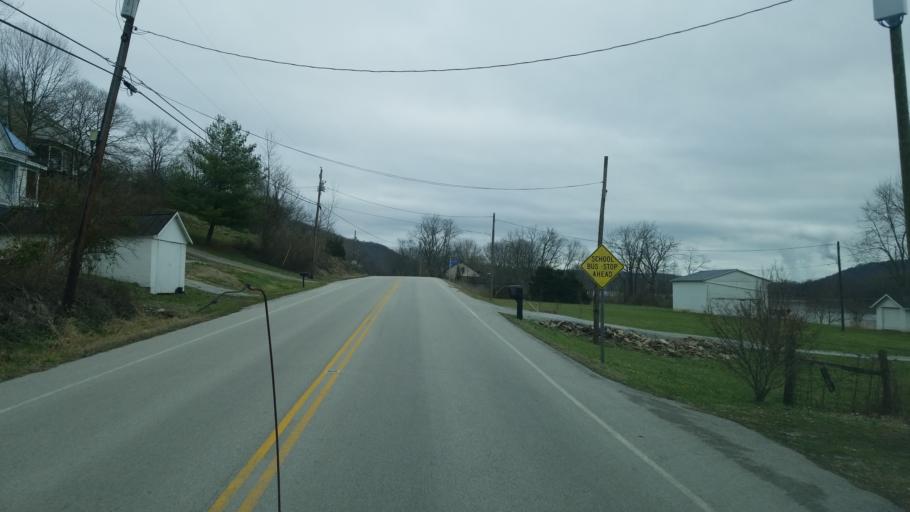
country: US
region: Ohio
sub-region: Brown County
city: Ripley
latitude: 38.7661
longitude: -83.8826
